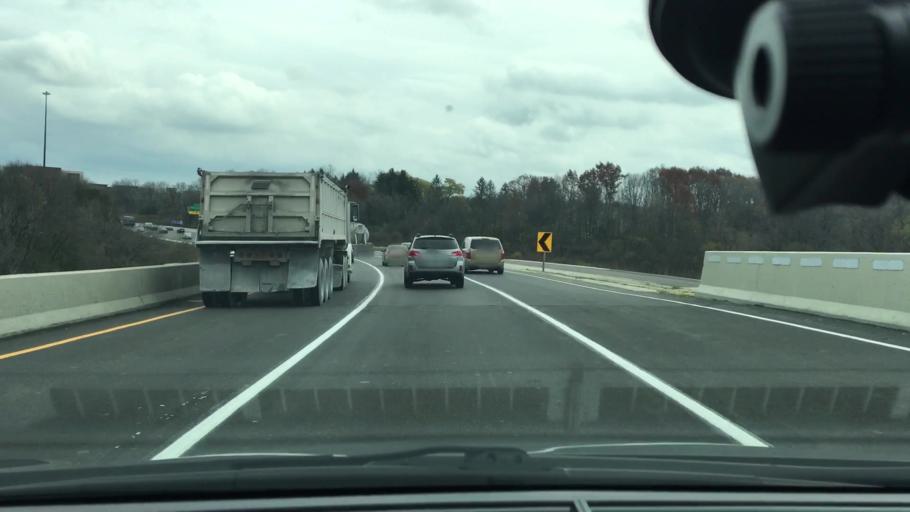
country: US
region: Wisconsin
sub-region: Milwaukee County
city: Greenfield
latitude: 42.9624
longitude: -88.0363
